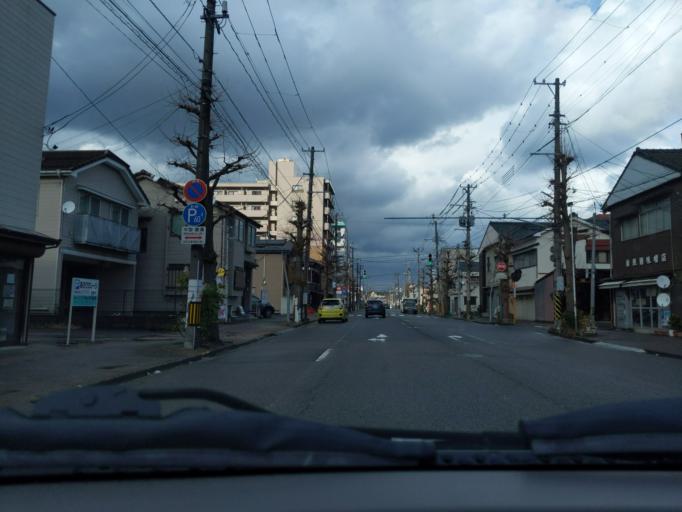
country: JP
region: Niigata
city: Niigata-shi
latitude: 37.9270
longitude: 139.0470
